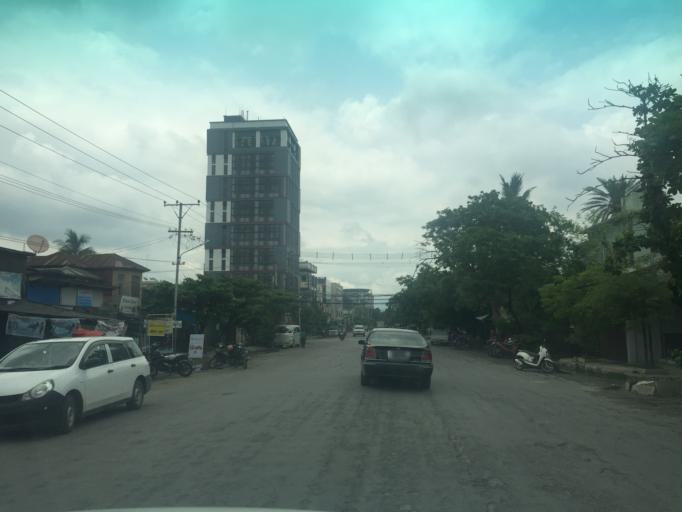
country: MM
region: Mandalay
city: Mandalay
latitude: 21.9710
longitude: 96.0813
